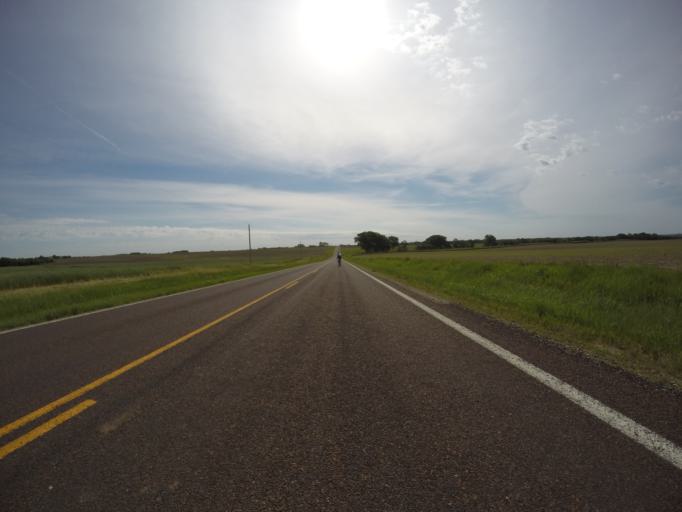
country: US
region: Kansas
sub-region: Washington County
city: Washington
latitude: 39.7118
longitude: -97.2357
